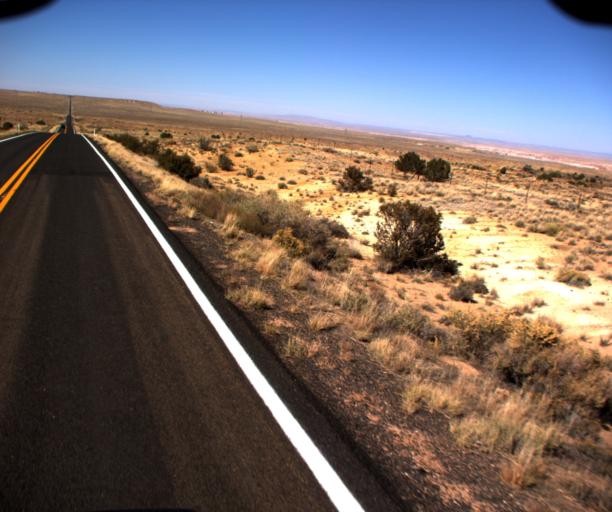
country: US
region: Arizona
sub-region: Coconino County
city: Tuba City
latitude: 35.9312
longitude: -110.8929
